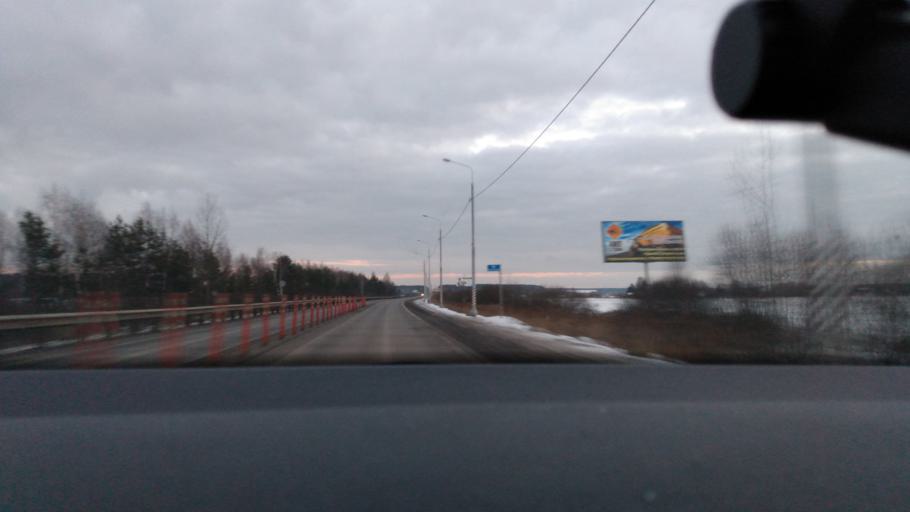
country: RU
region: Moskovskaya
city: Yegor'yevsk
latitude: 55.4450
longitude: 39.0145
